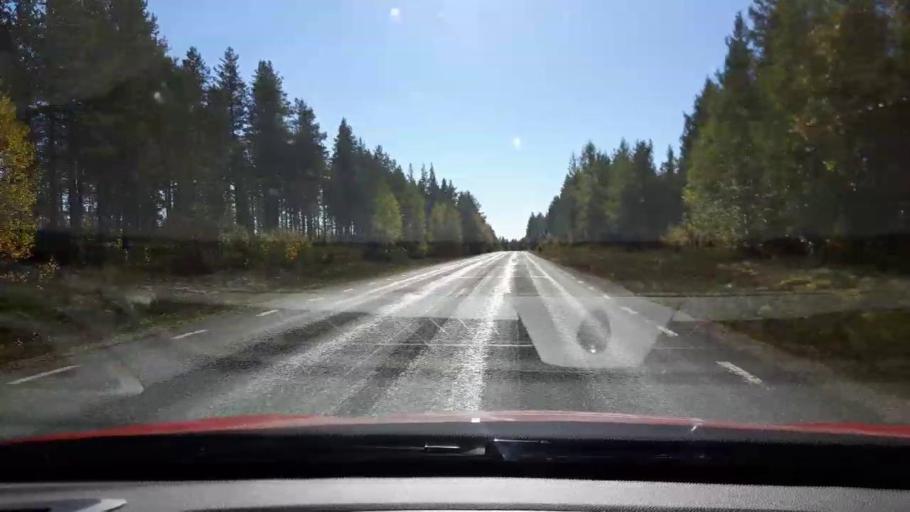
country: SE
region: Jaemtland
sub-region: Harjedalens Kommun
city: Sveg
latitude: 62.3450
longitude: 14.0353
